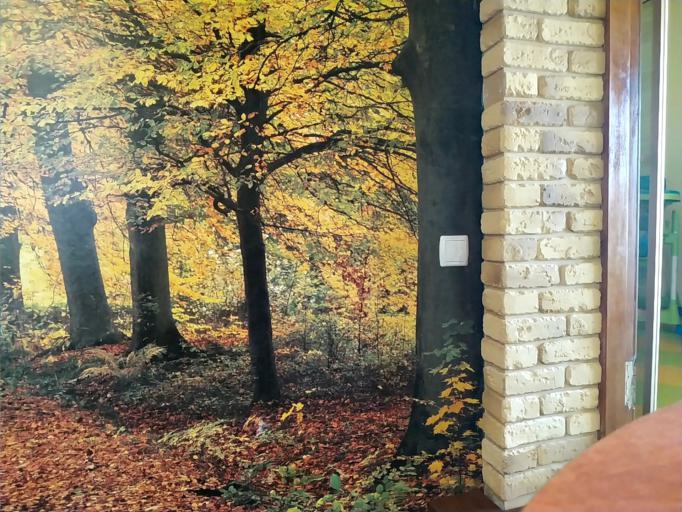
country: RU
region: Tverskaya
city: Maksatikha
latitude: 57.6099
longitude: 35.8270
